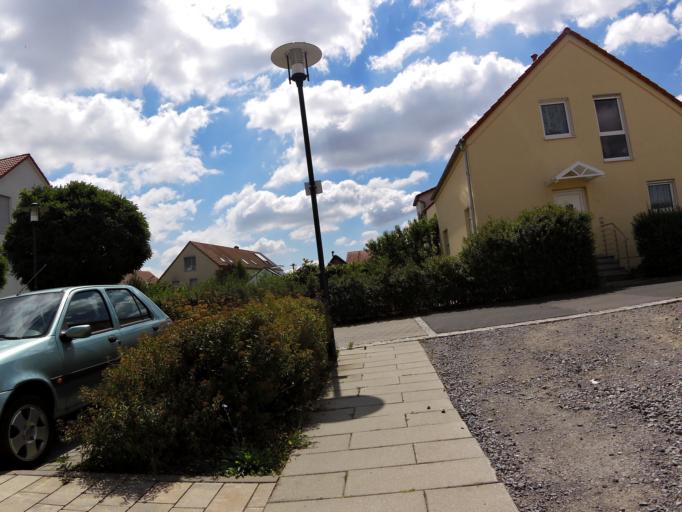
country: DE
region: Bavaria
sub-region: Regierungsbezirk Unterfranken
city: Gerbrunn
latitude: 49.7844
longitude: 9.9914
